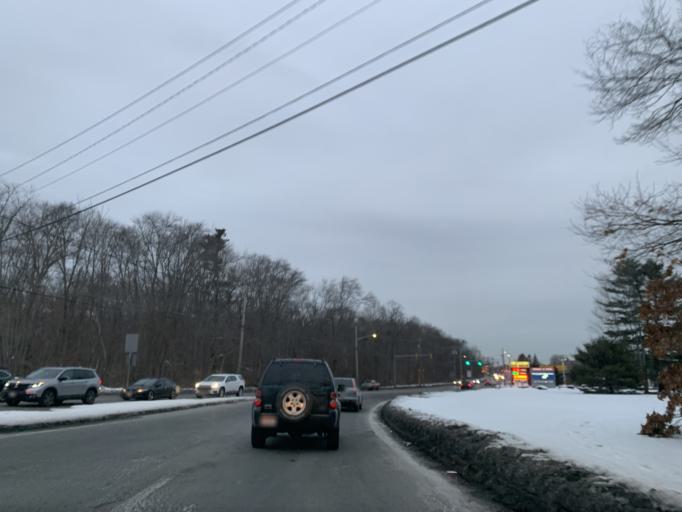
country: US
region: Massachusetts
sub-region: Norfolk County
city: Avon
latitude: 42.0966
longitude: -71.0652
